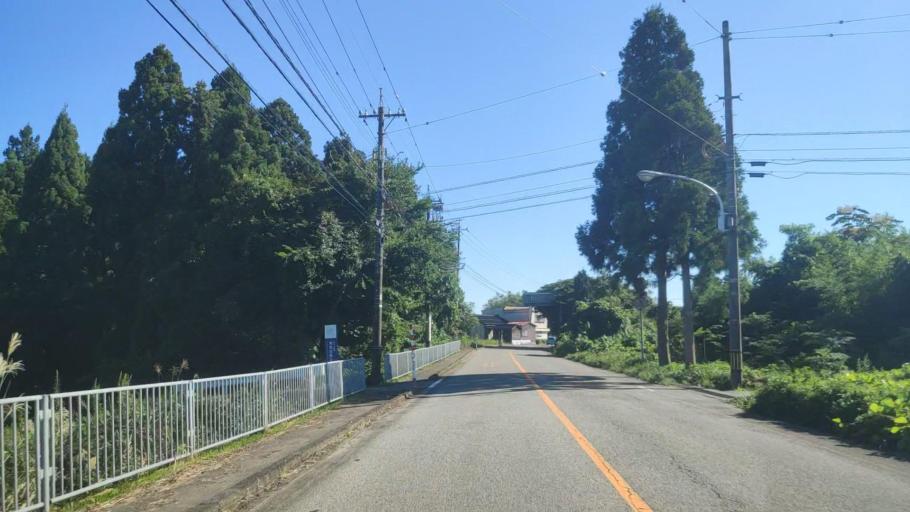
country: JP
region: Ishikawa
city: Nanao
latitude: 37.2586
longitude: 137.0892
